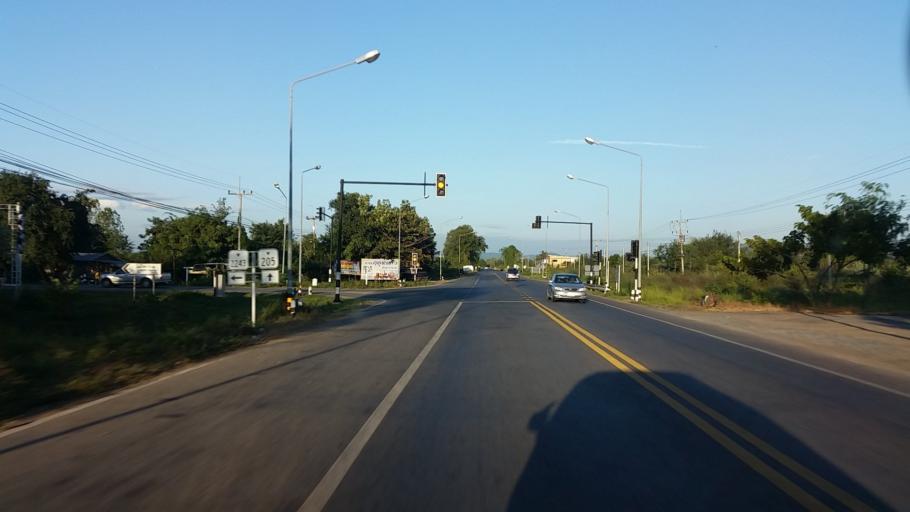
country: TH
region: Lop Buri
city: Chai Badan
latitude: 15.2643
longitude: 101.2045
